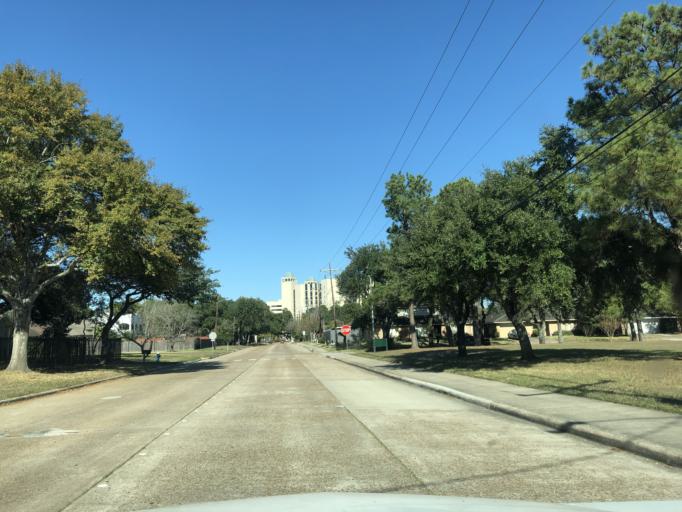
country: US
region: Texas
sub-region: Harris County
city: Bellaire
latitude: 29.6884
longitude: -95.5218
